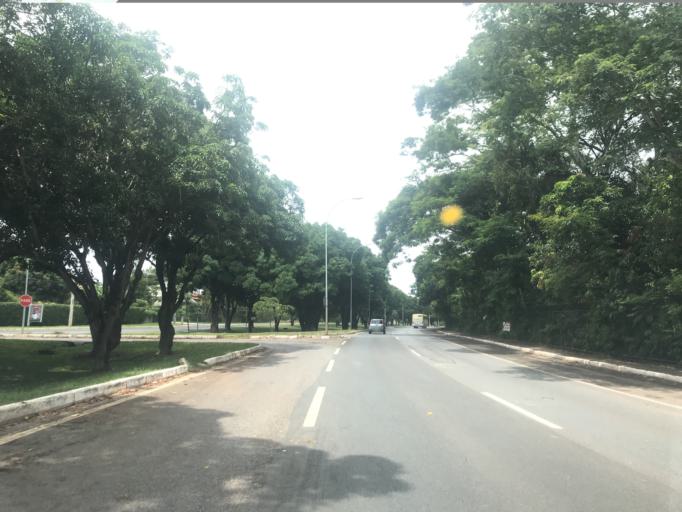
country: BR
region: Federal District
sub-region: Brasilia
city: Brasilia
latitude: -15.8409
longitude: -47.8399
